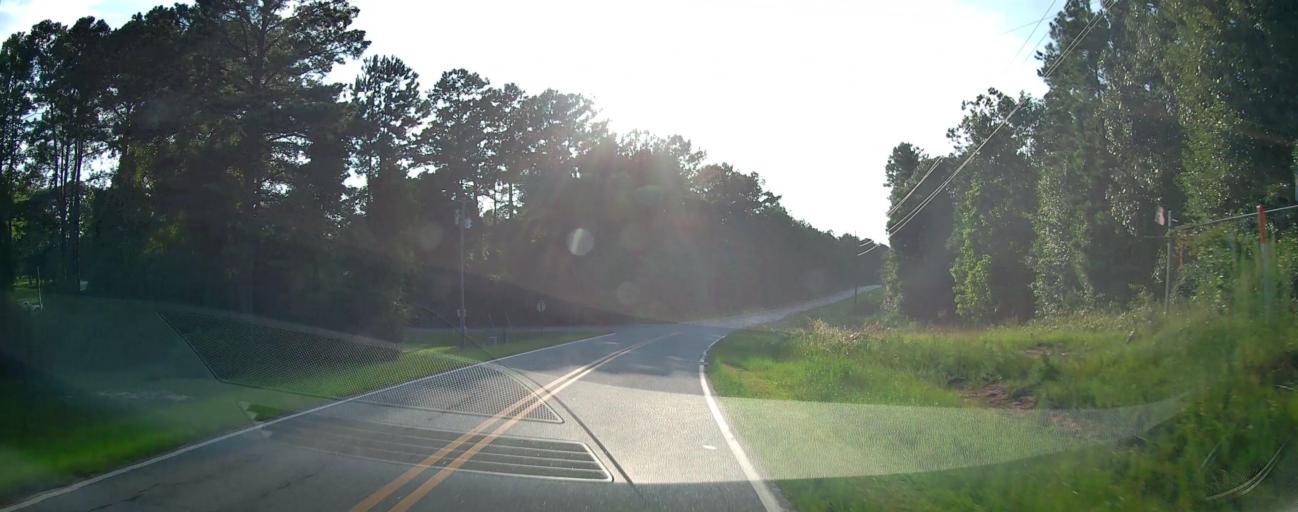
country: US
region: Georgia
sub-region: Peach County
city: Byron
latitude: 32.7055
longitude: -83.8326
